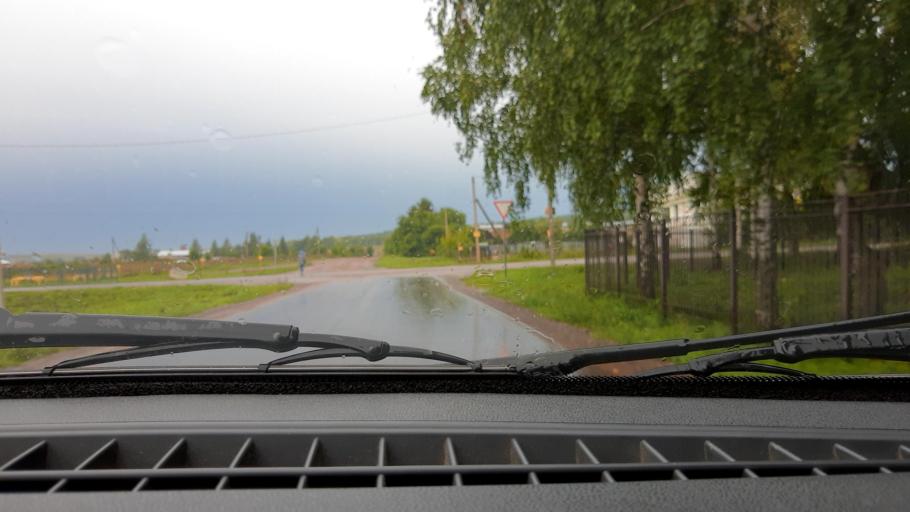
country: RU
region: Bashkortostan
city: Avdon
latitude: 54.8206
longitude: 55.6933
